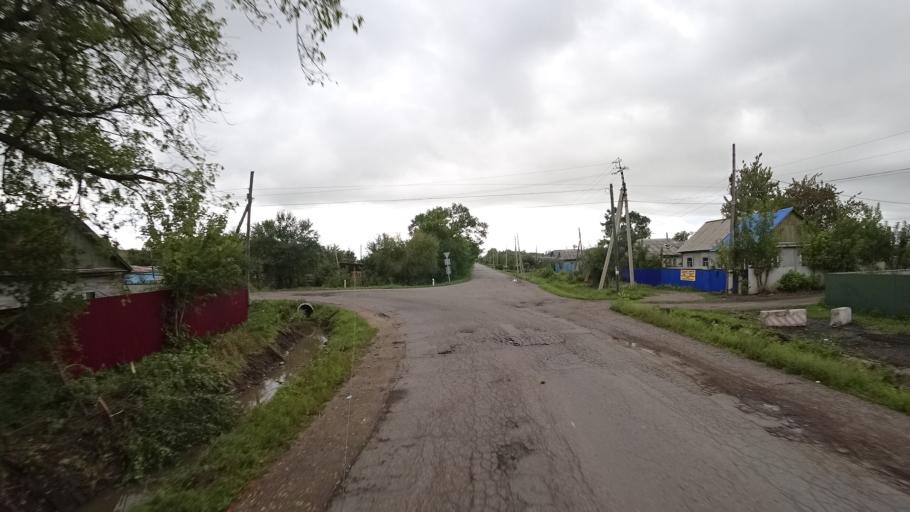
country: RU
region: Primorskiy
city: Chernigovka
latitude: 44.3502
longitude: 132.5679
